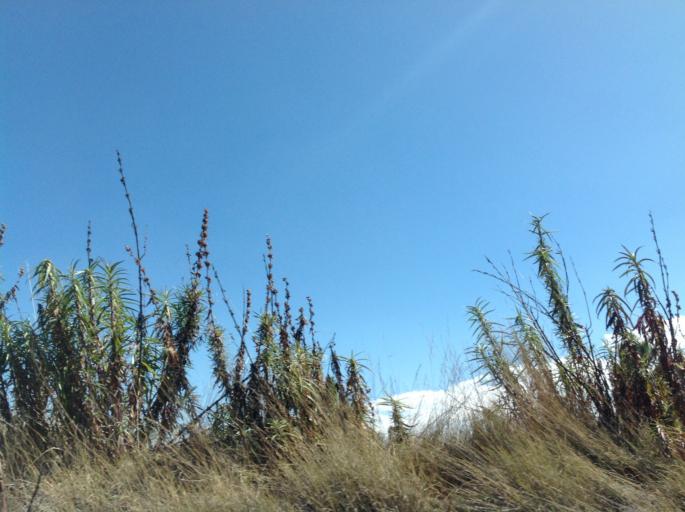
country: MX
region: Mexico
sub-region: Amecameca
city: San Diego Huehuecalco
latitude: 19.1047
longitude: -98.6458
